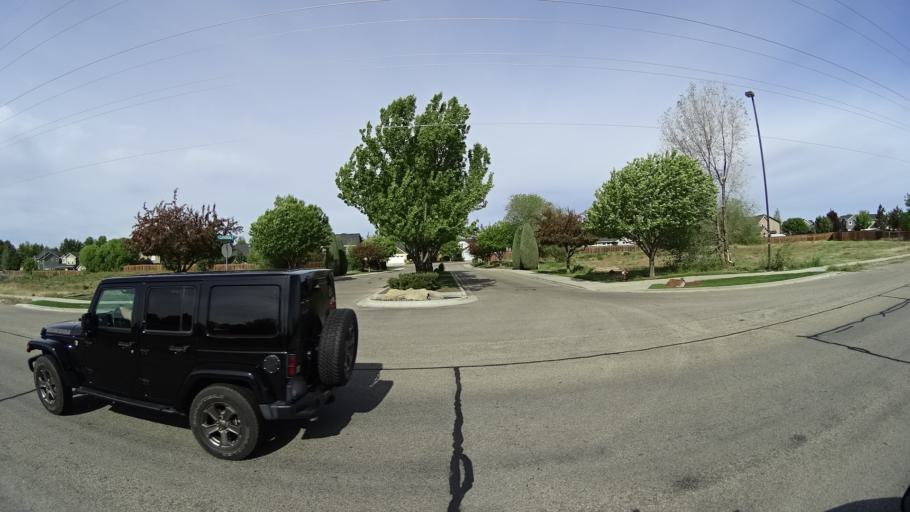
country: US
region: Idaho
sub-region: Ada County
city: Meridian
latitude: 43.5476
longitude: -116.3341
